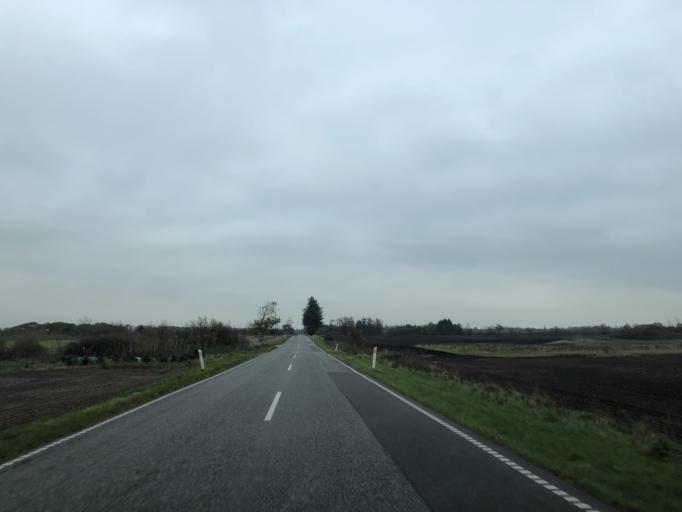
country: DK
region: Central Jutland
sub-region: Holstebro Kommune
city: Ulfborg
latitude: 56.1938
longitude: 8.3448
